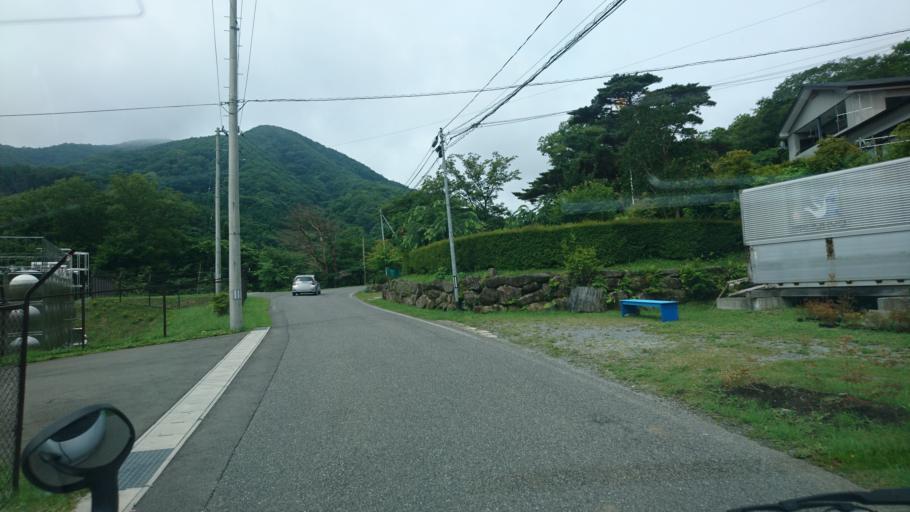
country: JP
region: Iwate
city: Ofunato
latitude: 39.1350
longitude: 141.7841
